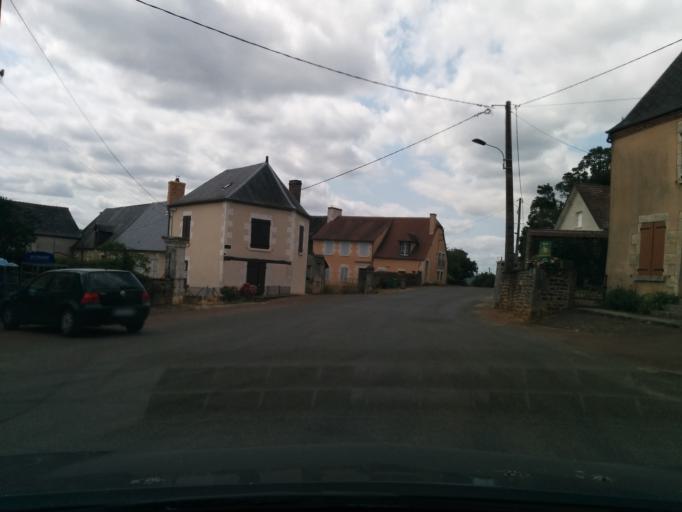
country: FR
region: Centre
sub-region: Departement du Cher
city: Sancerre
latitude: 47.3268
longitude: 2.7078
